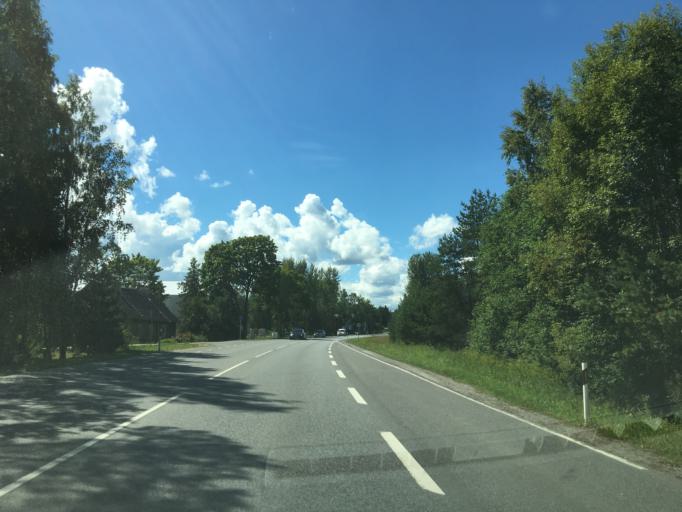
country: EE
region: Harju
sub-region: Nissi vald
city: Riisipere
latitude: 59.2382
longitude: 24.2744
